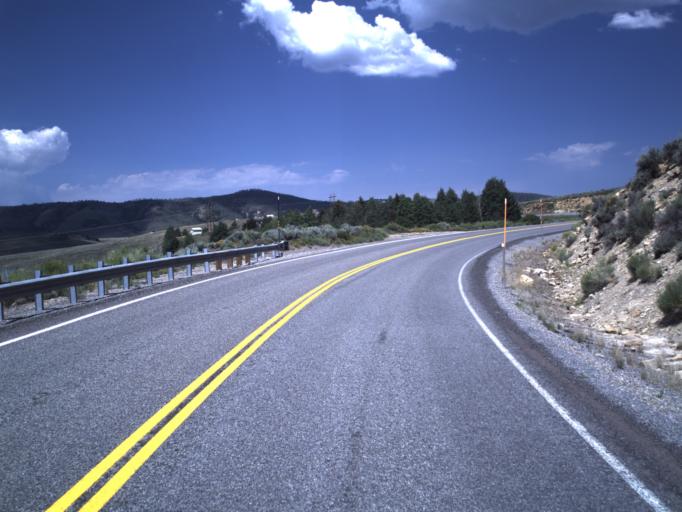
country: US
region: Utah
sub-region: Carbon County
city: Helper
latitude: 39.7889
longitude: -111.1275
